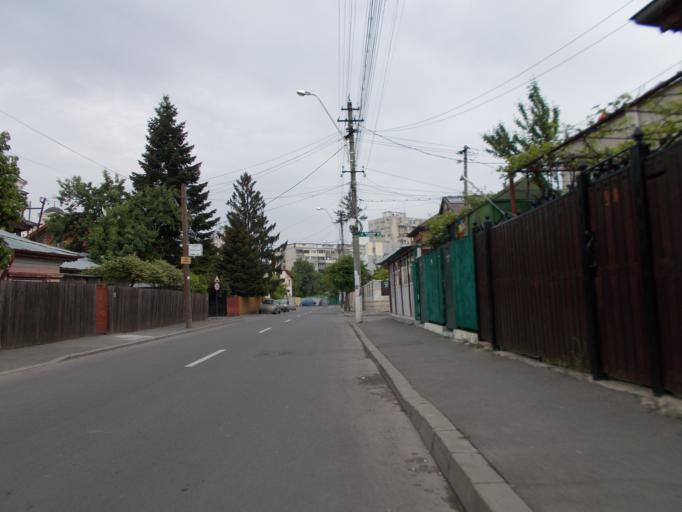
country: RO
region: Bucuresti
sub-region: Municipiul Bucuresti
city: Bucuresti
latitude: 44.3888
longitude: 26.0958
